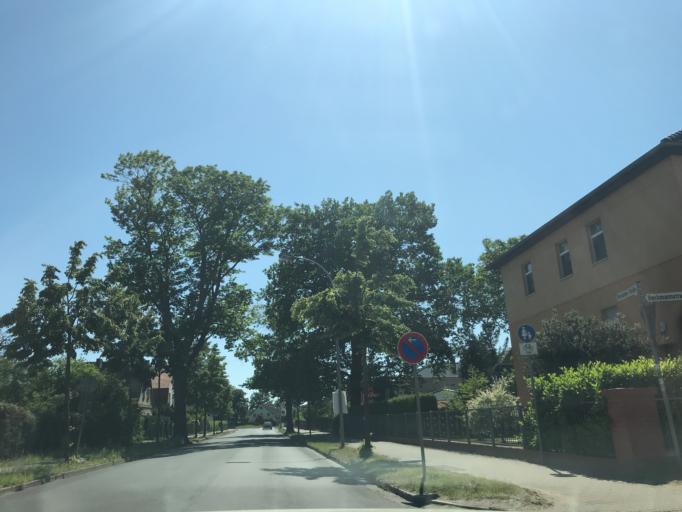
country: DE
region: Brandenburg
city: Falkensee
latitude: 52.5547
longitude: 13.0883
